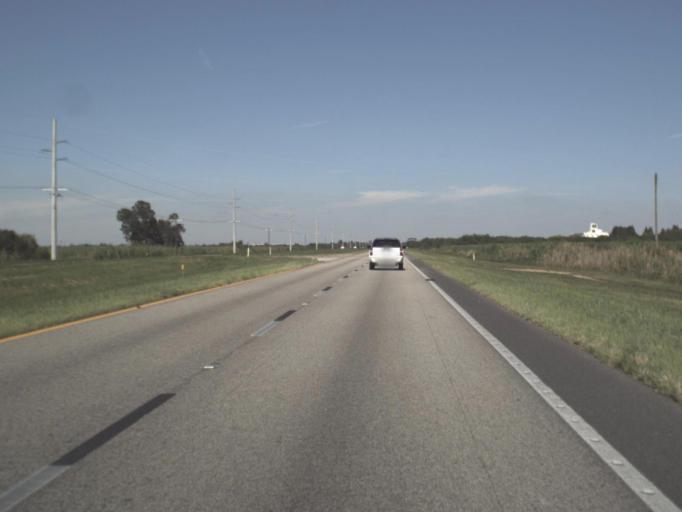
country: US
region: Florida
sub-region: Glades County
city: Moore Haven
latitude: 26.7924
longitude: -81.0826
